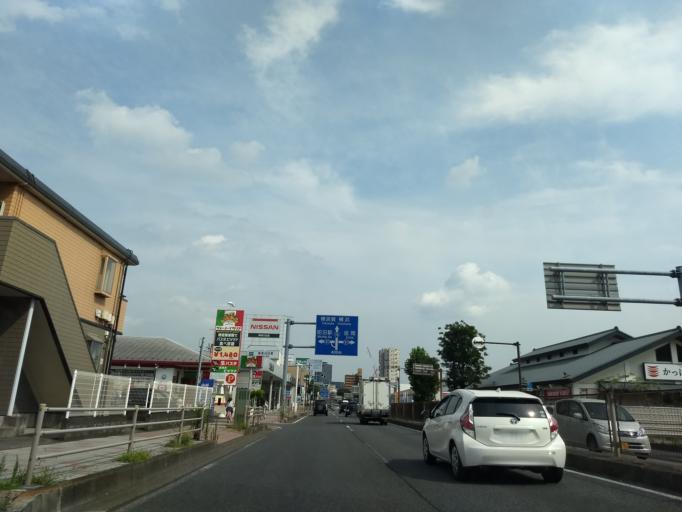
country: JP
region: Tokyo
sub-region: Machida-shi
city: Machida
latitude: 35.5402
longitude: 139.4326
